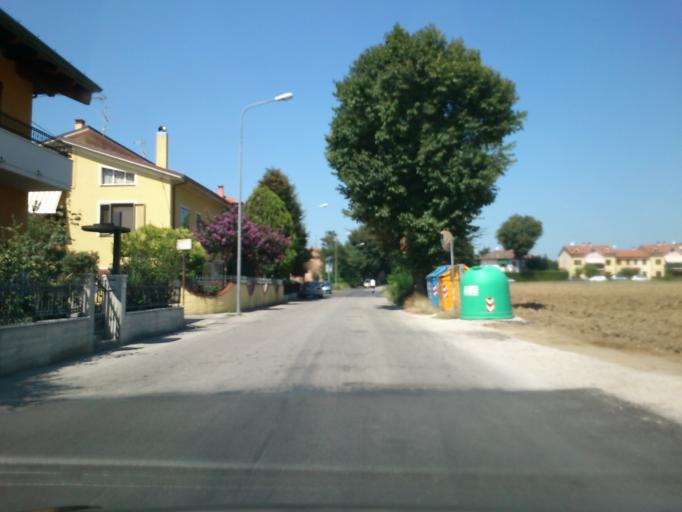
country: IT
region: The Marches
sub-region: Provincia di Pesaro e Urbino
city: Lucrezia
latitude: 43.7712
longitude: 12.9457
